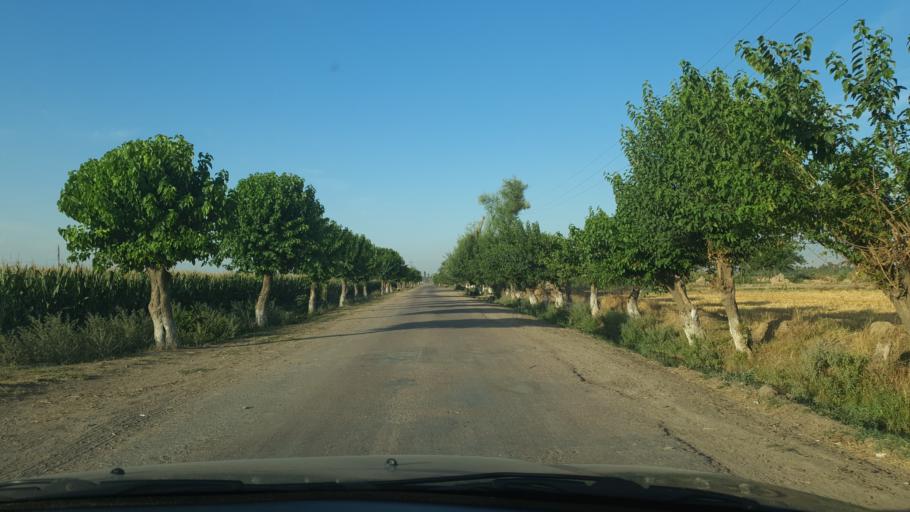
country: UZ
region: Toshkent
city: Tuytepa
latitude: 41.1006
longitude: 69.3820
